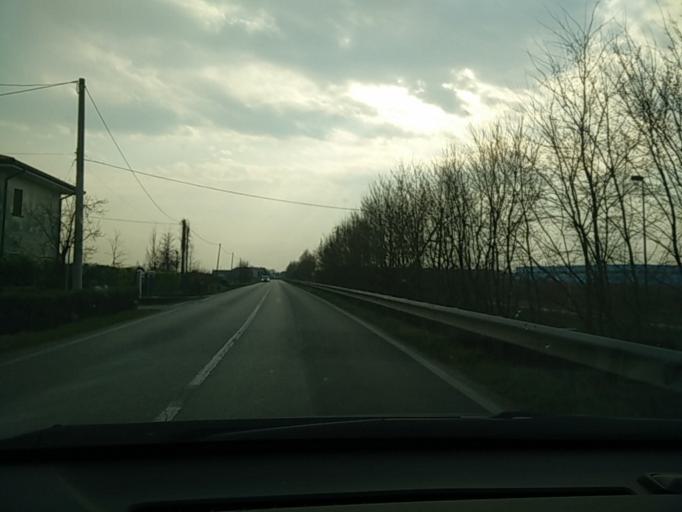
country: IT
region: Veneto
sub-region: Provincia di Treviso
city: Codogne
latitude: 45.8569
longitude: 12.4009
